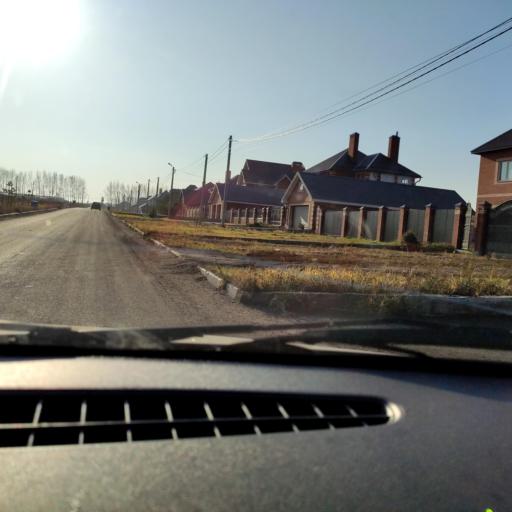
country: RU
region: Bashkortostan
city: Kabakovo
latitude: 54.6189
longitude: 56.1416
